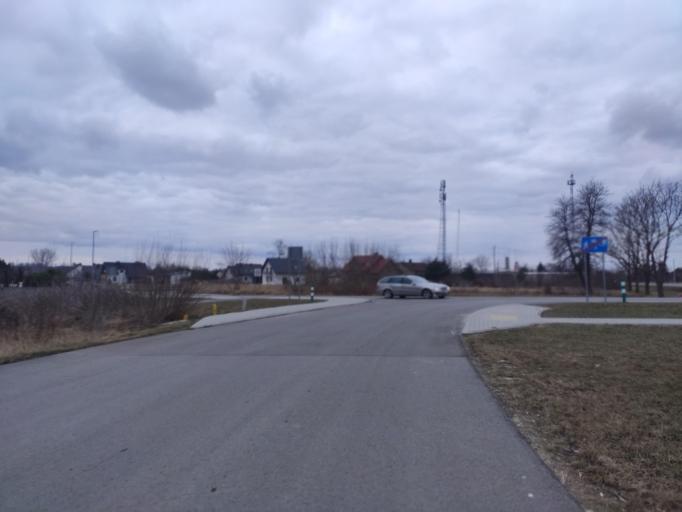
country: PL
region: Lublin Voivodeship
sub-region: Powiat lubartowski
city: Kock
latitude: 51.6426
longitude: 22.4307
